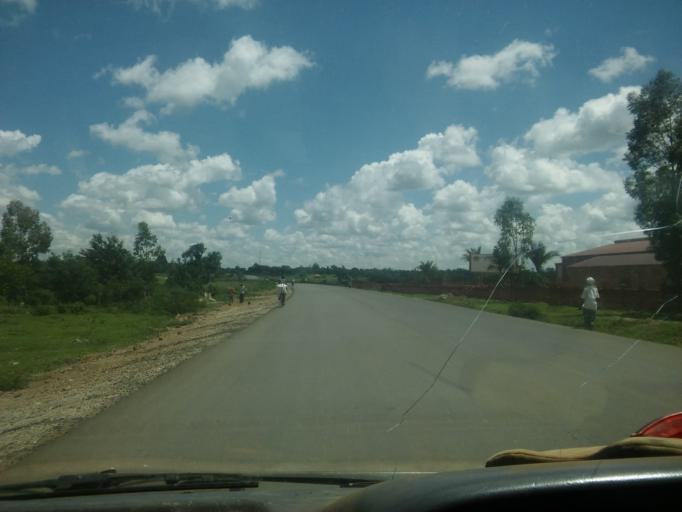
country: UG
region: Eastern Region
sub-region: Mbale District
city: Mbale
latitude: 1.0758
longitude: 34.1090
